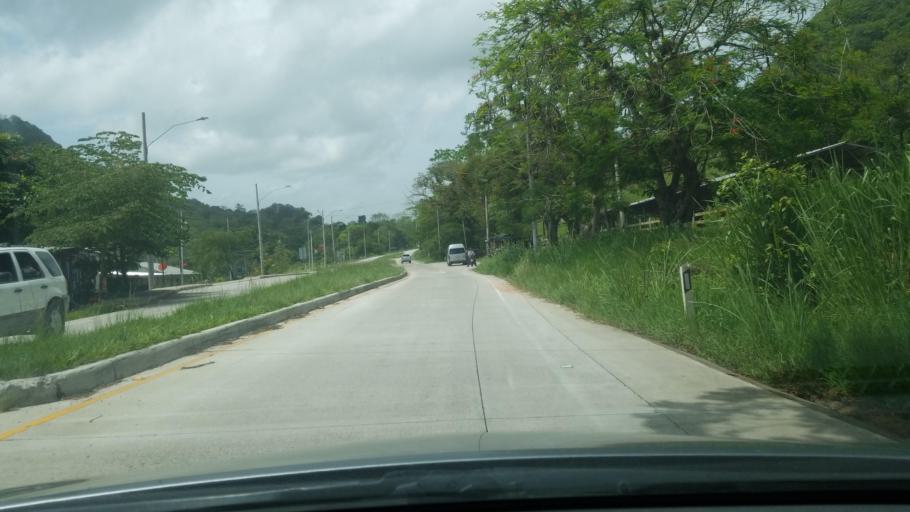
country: HN
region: Copan
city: Trinidad de Copan
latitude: 14.9504
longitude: -88.7661
